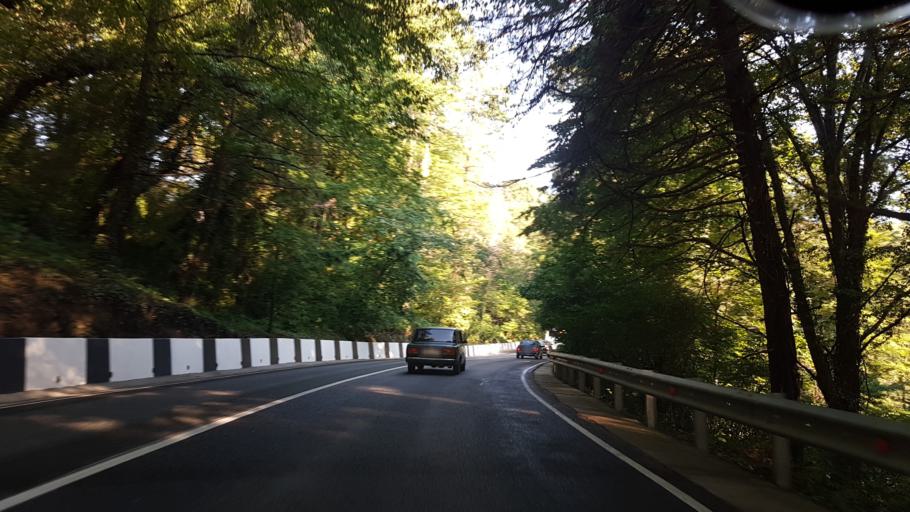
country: RU
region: Krasnodarskiy
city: Dagomys
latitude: 43.6605
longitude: 39.6387
